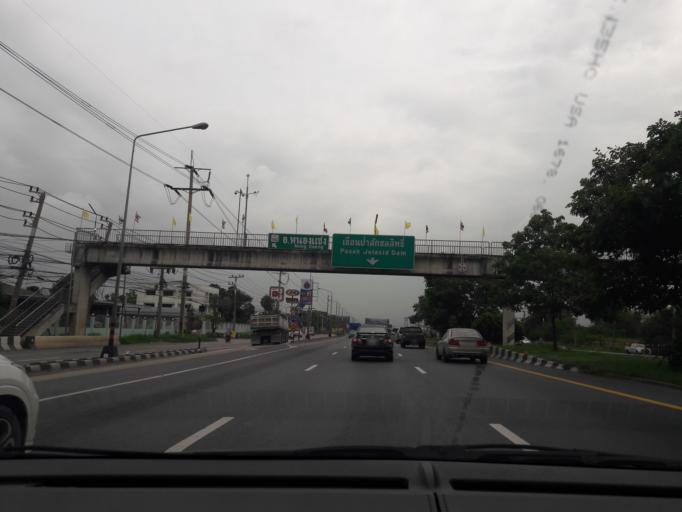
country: TH
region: Sara Buri
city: Nong Khae
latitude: 14.4288
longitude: 100.8949
